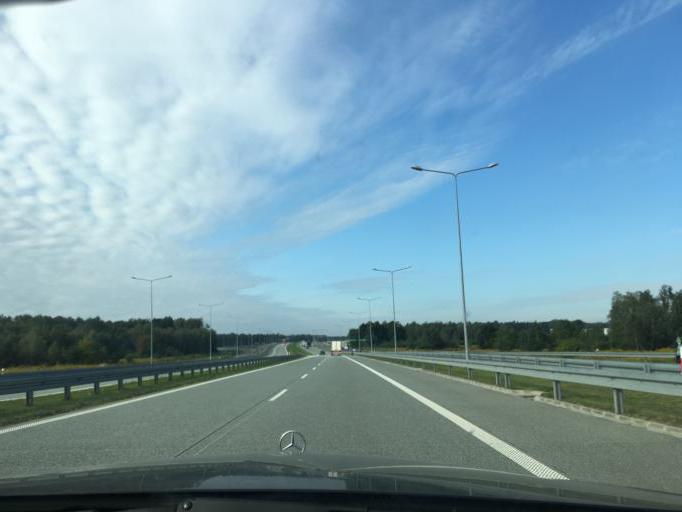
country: PL
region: Lodz Voivodeship
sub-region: Powiat lodzki wschodni
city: Rzgow
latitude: 51.6415
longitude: 19.5089
